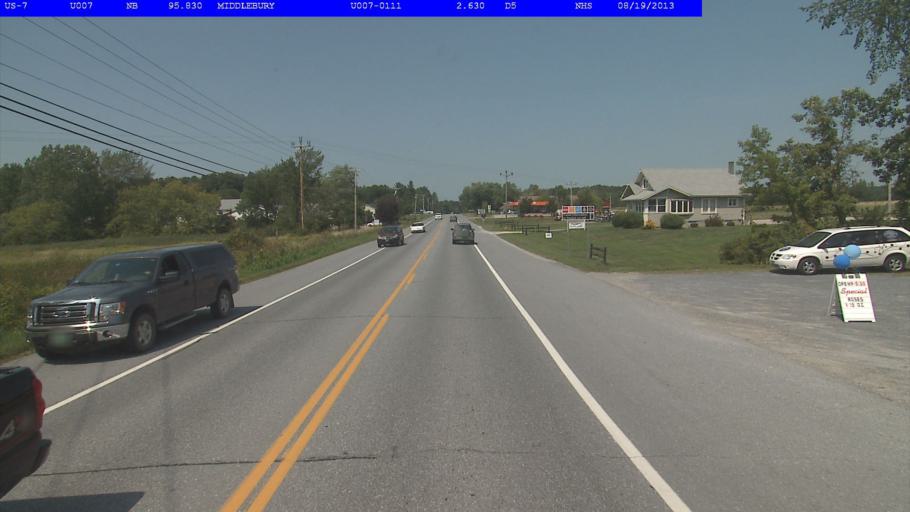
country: US
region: Vermont
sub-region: Addison County
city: Middlebury (village)
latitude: 43.9884
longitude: -73.1356
